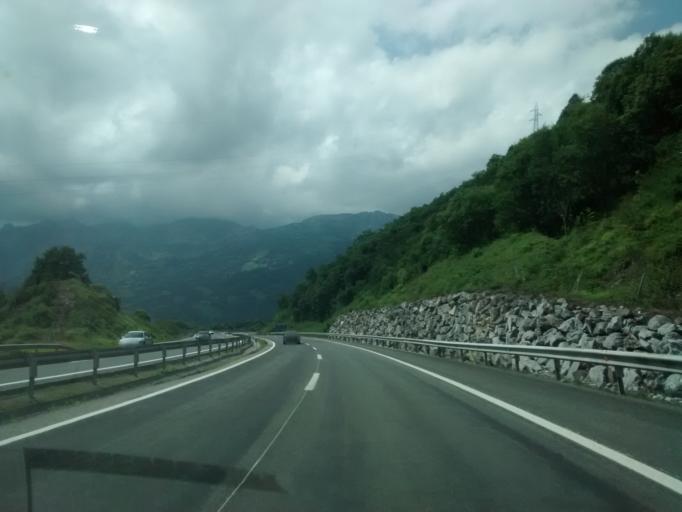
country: ES
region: Asturias
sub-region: Province of Asturias
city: Pola de Lena
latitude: 43.0191
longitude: -5.8176
